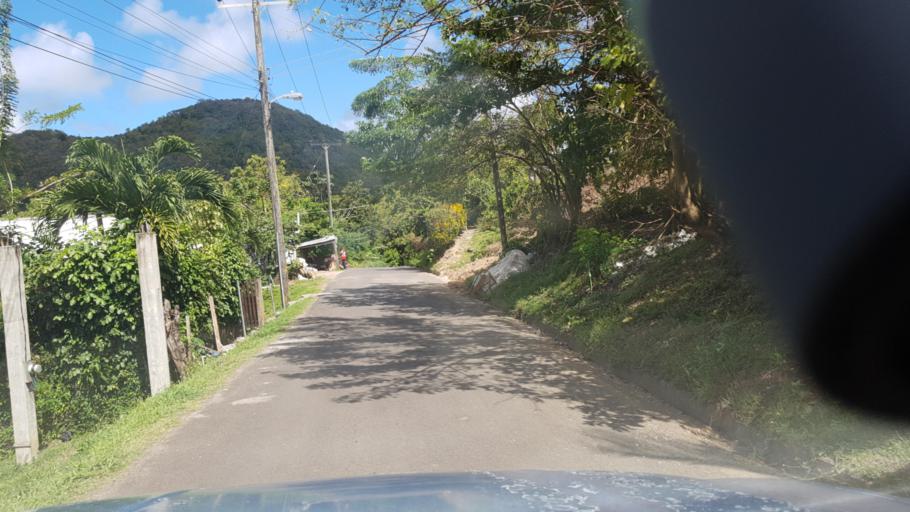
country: LC
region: Gros-Islet
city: Gros Islet
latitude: 14.0458
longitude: -60.9492
